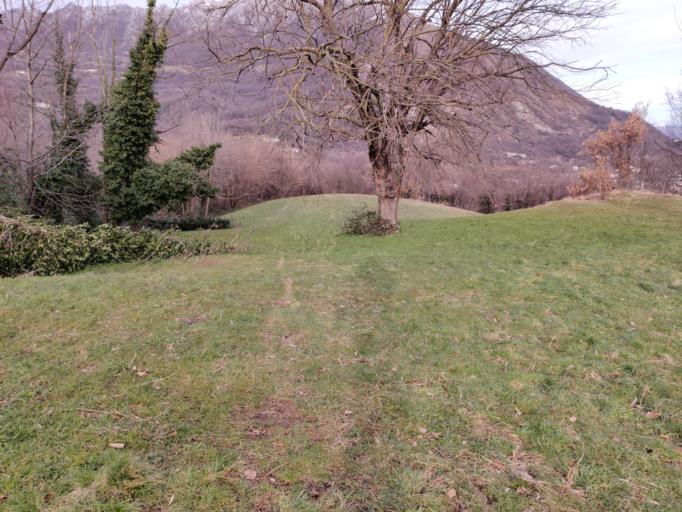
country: IT
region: Veneto
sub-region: Provincia di Vicenza
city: Santorso
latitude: 45.7336
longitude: 11.3661
